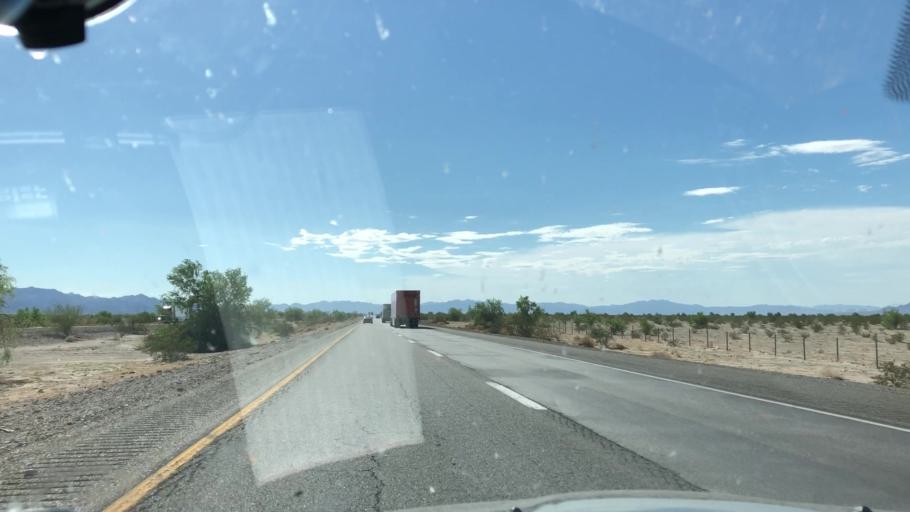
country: US
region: California
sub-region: Riverside County
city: Mesa Verde
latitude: 33.6582
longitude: -115.1609
